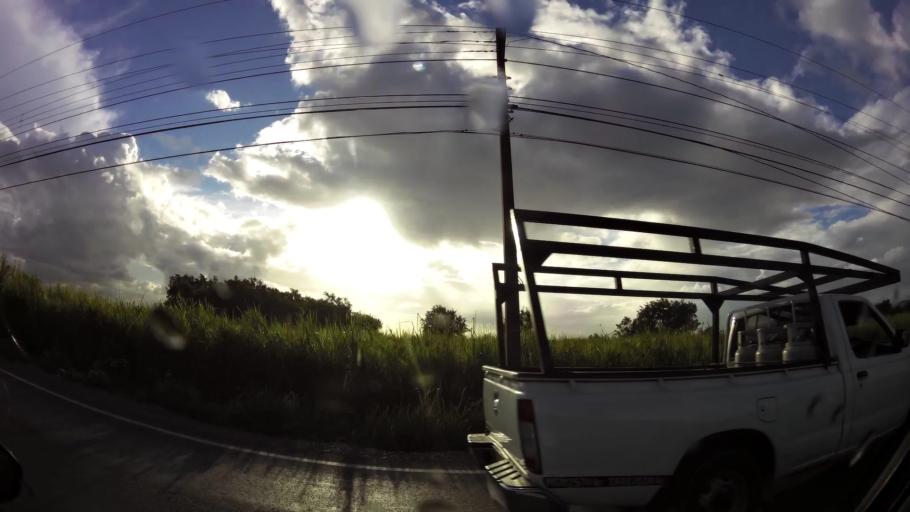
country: TT
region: Tunapuna/Piarco
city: Tunapuna
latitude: 10.5950
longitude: -61.3678
